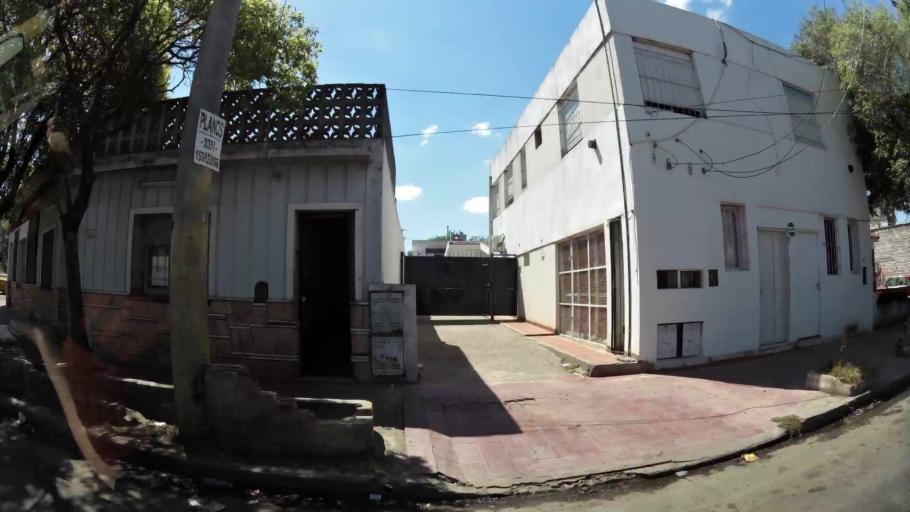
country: AR
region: Cordoba
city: Villa Allende
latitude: -31.3358
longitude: -64.2620
